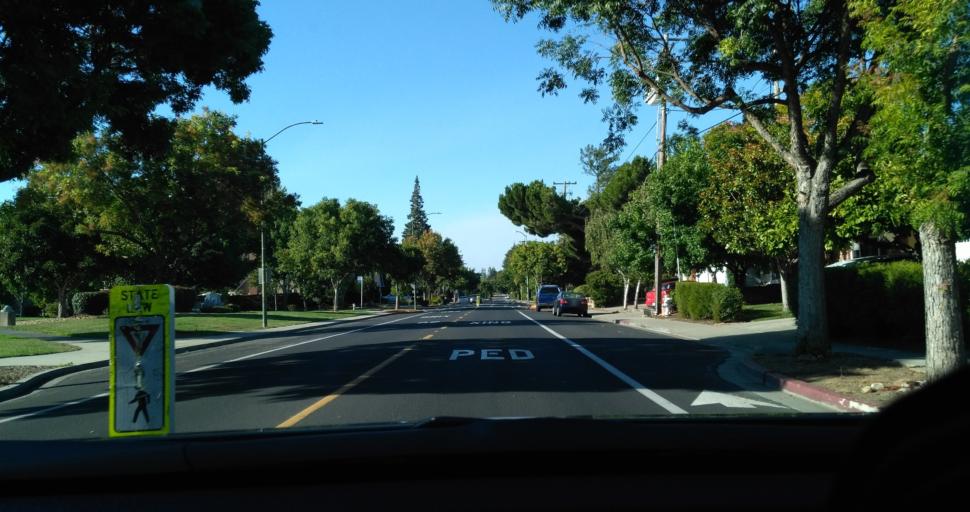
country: US
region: California
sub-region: Santa Clara County
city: Mountain View
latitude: 37.3813
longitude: -122.0619
